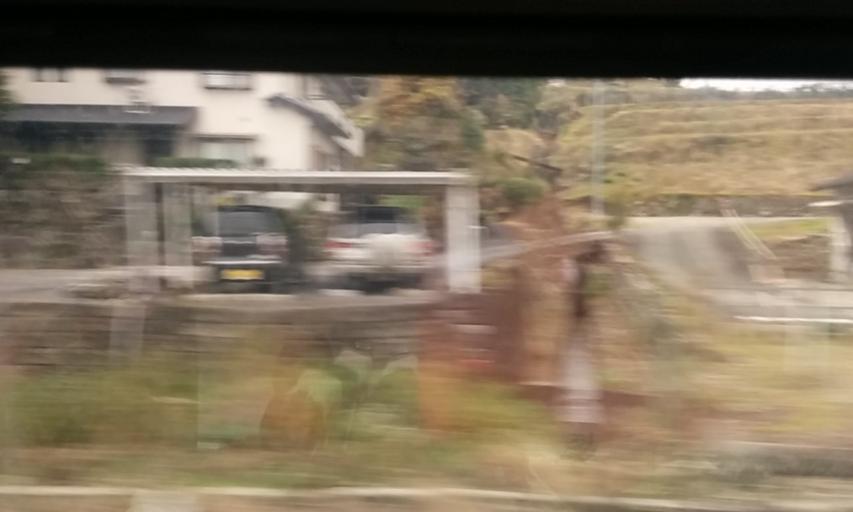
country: JP
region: Gifu
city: Nakatsugawa
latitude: 35.5231
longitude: 137.5294
